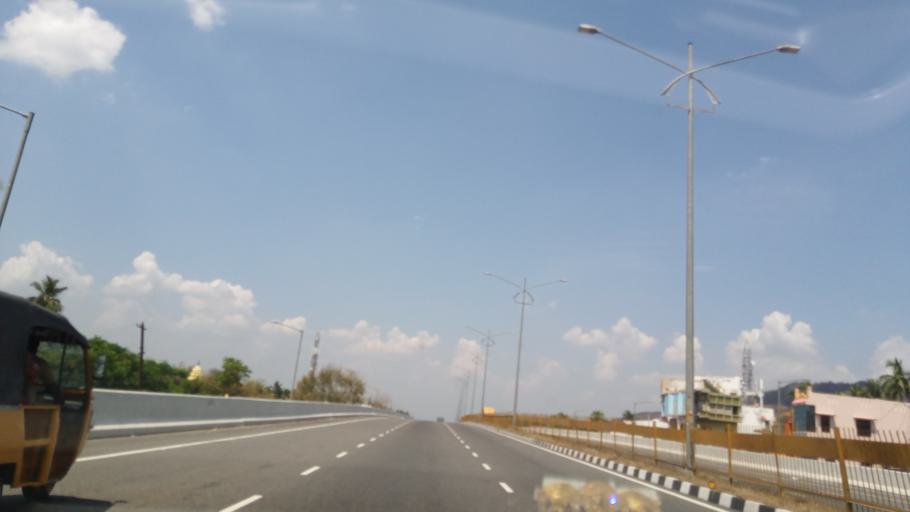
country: IN
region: Tamil Nadu
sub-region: Vellore
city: Gudiyatham
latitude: 12.8701
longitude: 78.8465
